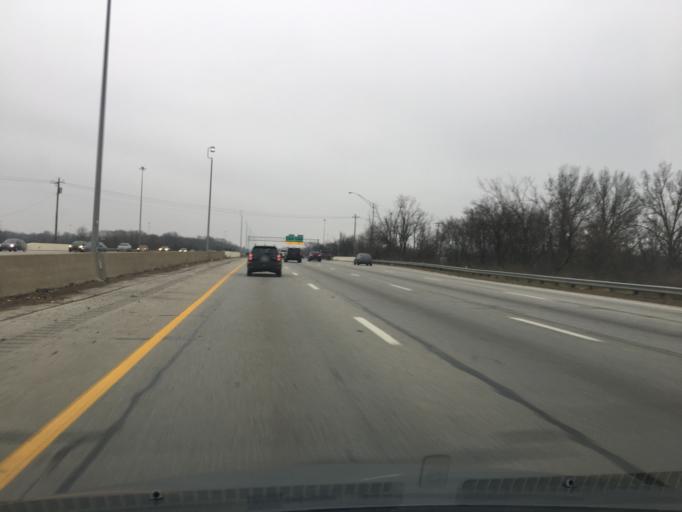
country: US
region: Ohio
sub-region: Hamilton County
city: Highpoint
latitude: 39.2768
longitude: -84.3590
